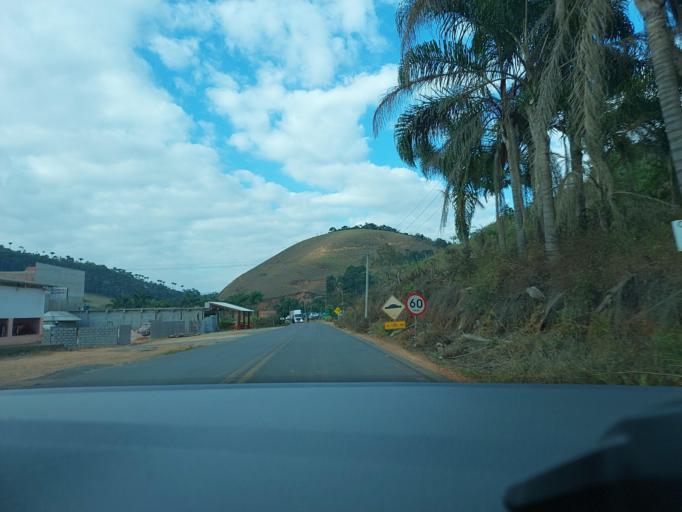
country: BR
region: Minas Gerais
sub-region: Vicosa
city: Vicosa
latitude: -20.8439
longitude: -42.6783
